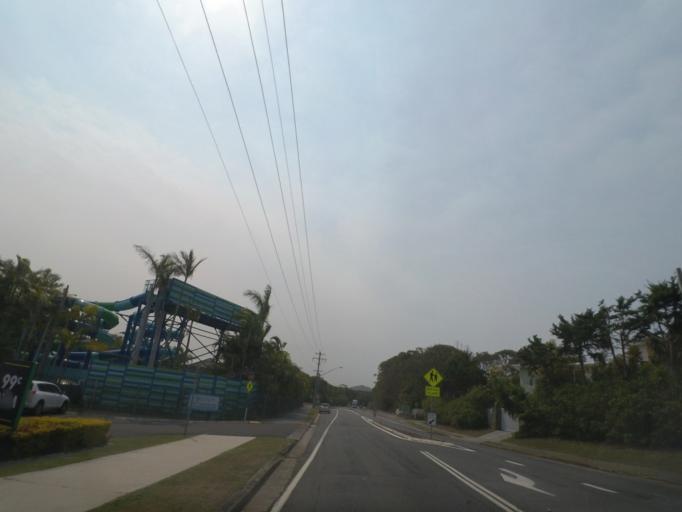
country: AU
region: New South Wales
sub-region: Tweed
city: Pottsville Beach
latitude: -28.3554
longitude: 153.5732
